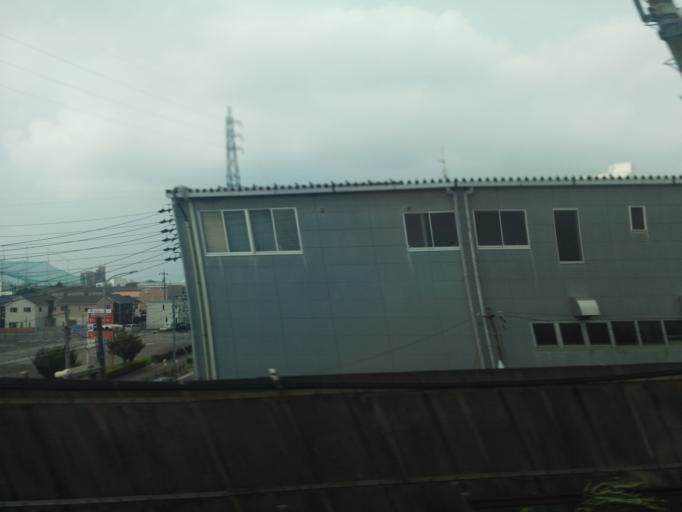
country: JP
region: Aichi
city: Chiryu
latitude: 35.0015
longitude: 137.0209
